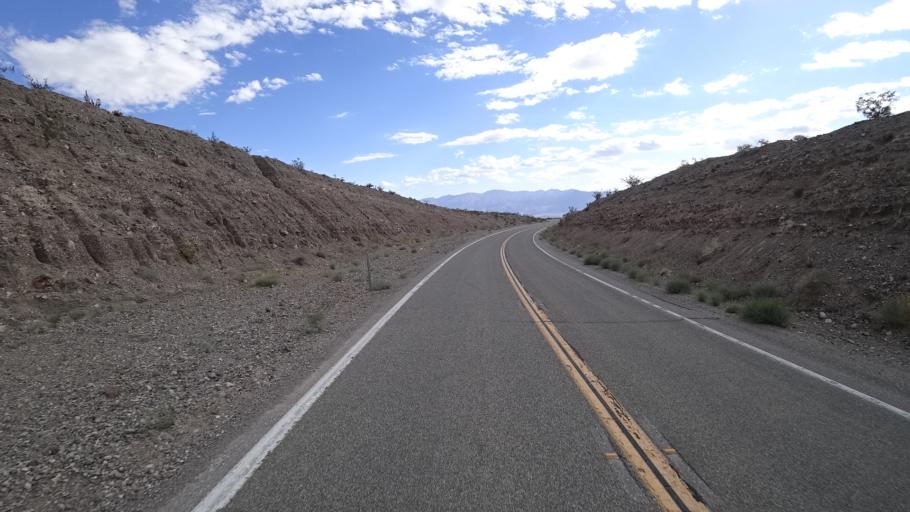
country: US
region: California
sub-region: San Bernardino County
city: Searles Valley
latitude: 36.3524
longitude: -117.2950
